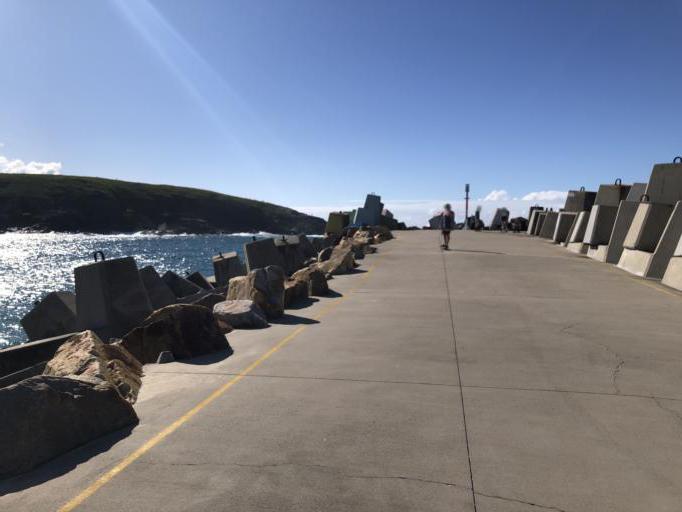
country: AU
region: New South Wales
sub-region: Coffs Harbour
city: Coffs Harbour
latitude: -30.3096
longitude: 153.1524
